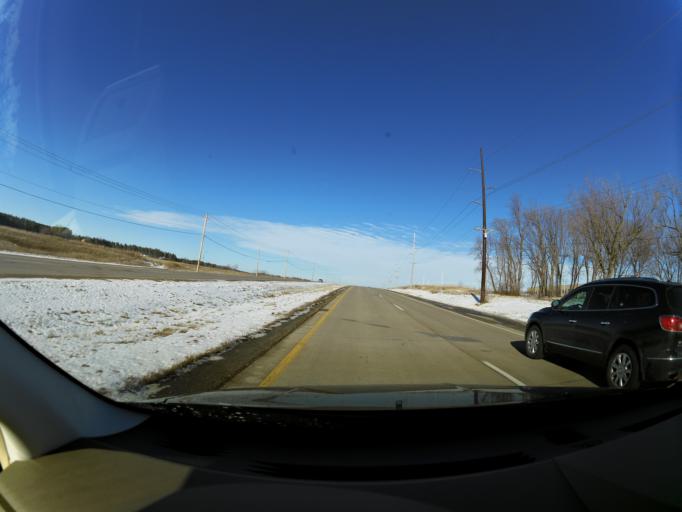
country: US
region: Minnesota
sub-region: Olmsted County
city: Rochester
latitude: 44.0645
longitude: -92.5238
